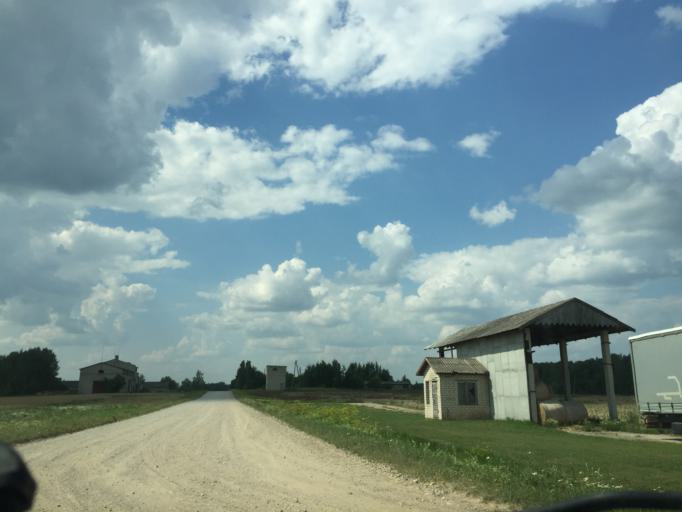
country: LT
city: Zagare
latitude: 56.3363
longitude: 23.0761
